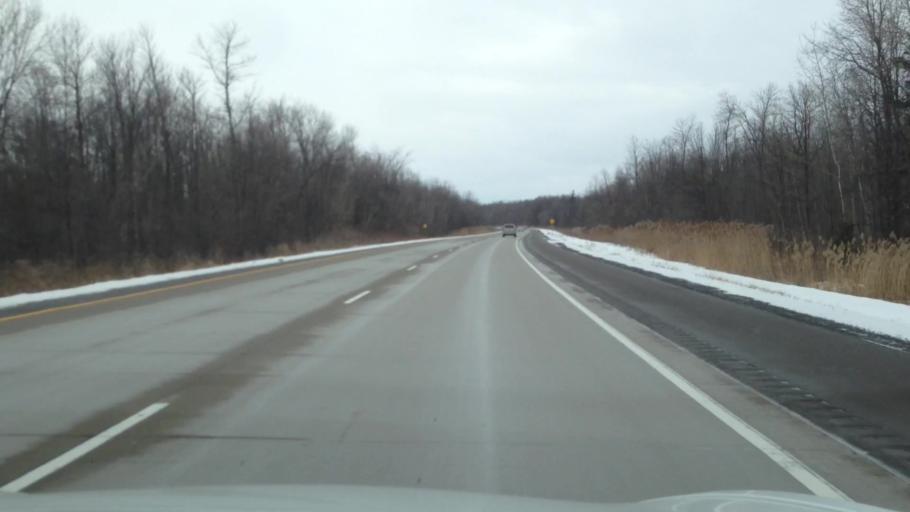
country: CA
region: Ontario
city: Hawkesbury
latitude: 45.4493
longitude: -74.7102
